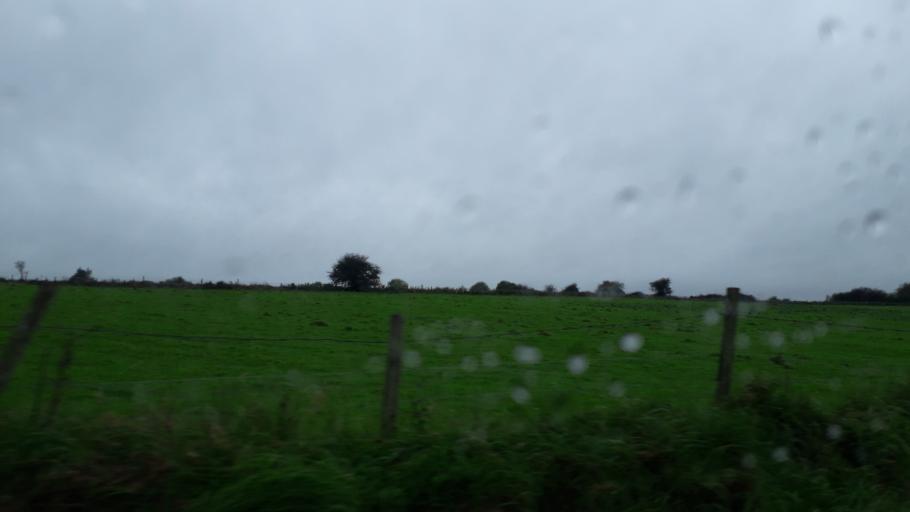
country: IE
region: Connaught
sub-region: Roscommon
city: Roscommon
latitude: 53.7812
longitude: -8.2588
